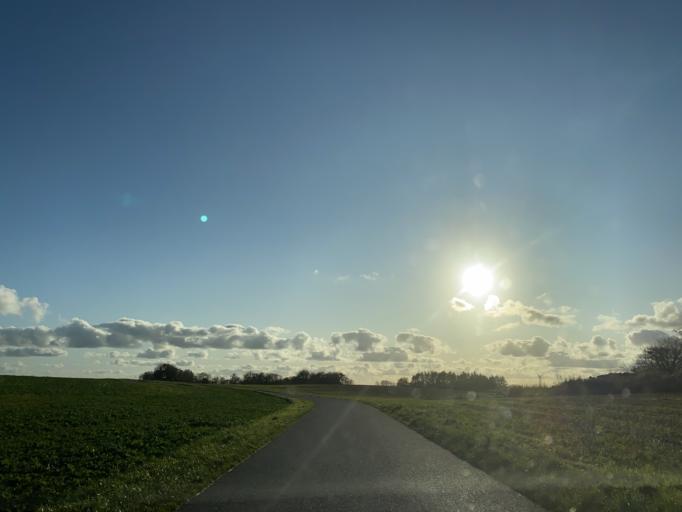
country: DK
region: Central Jutland
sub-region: Viborg Kommune
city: Bjerringbro
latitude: 56.3451
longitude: 9.7151
